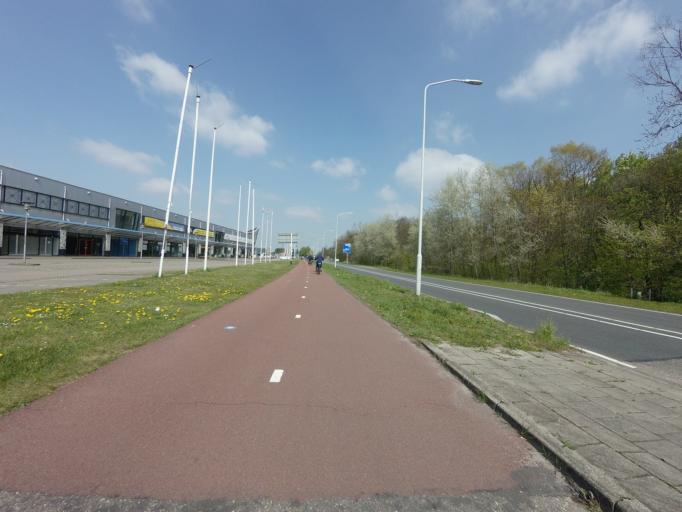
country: NL
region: North Holland
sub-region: Gemeente Zaanstad
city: Zaandam
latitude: 52.4223
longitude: 4.8272
